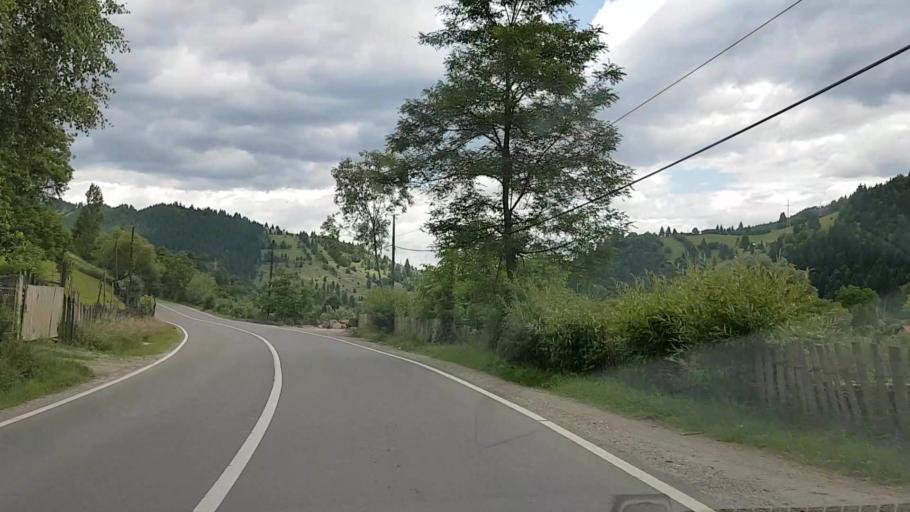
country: RO
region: Neamt
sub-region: Comuna Farcasa
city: Farcasa
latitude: 47.1595
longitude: 25.8238
